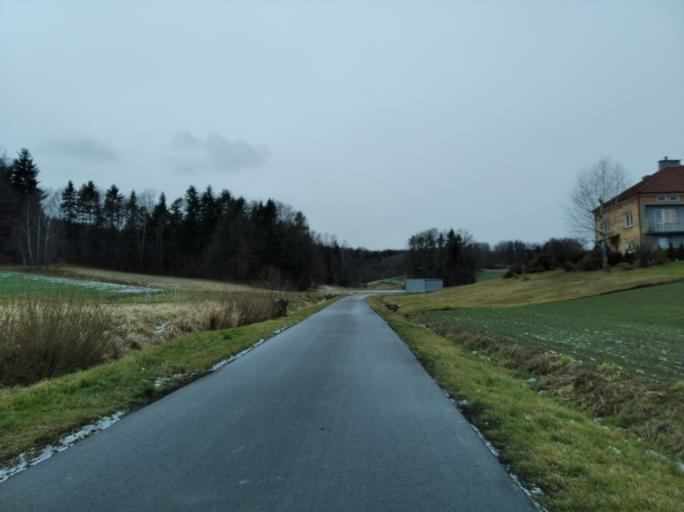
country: PL
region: Subcarpathian Voivodeship
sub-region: Powiat strzyzowski
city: Wysoka Strzyzowska
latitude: 49.9024
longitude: 21.7264
